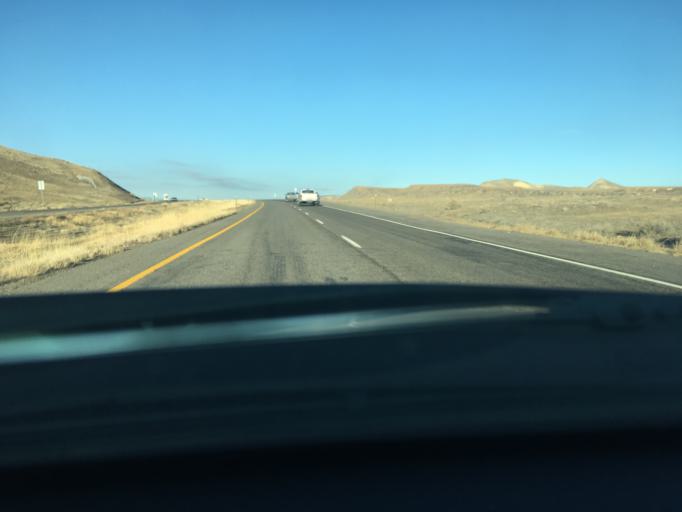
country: US
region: Colorado
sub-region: Delta County
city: Delta
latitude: 38.7542
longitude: -108.1707
